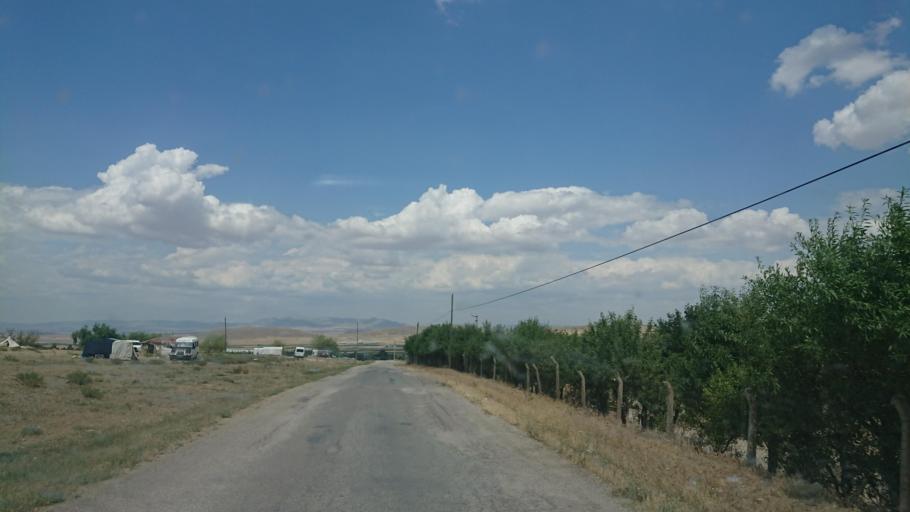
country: TR
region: Aksaray
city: Sariyahsi
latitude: 38.9626
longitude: 33.8881
